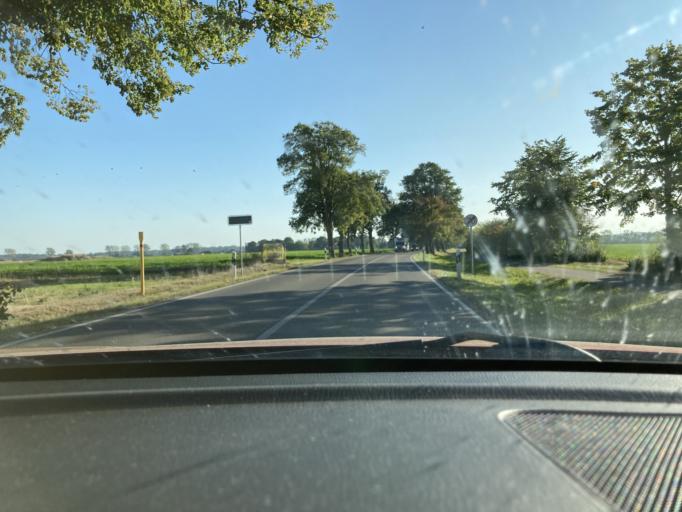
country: DE
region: Mecklenburg-Vorpommern
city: Anklam
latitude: 53.8170
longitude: 13.6807
